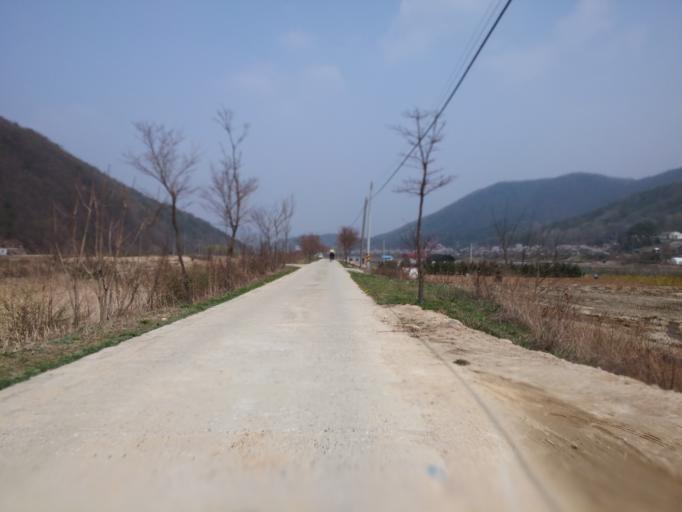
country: KR
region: Daejeon
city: Songgang-dong
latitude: 36.3767
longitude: 127.2578
